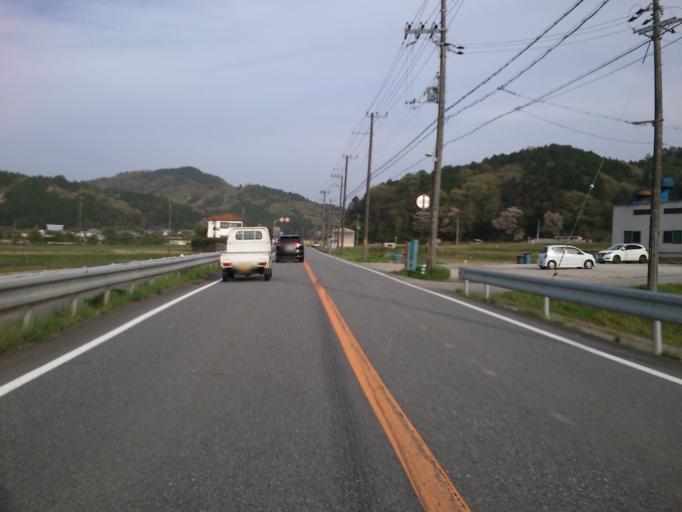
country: JP
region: Hyogo
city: Sasayama
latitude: 35.0794
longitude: 135.3274
